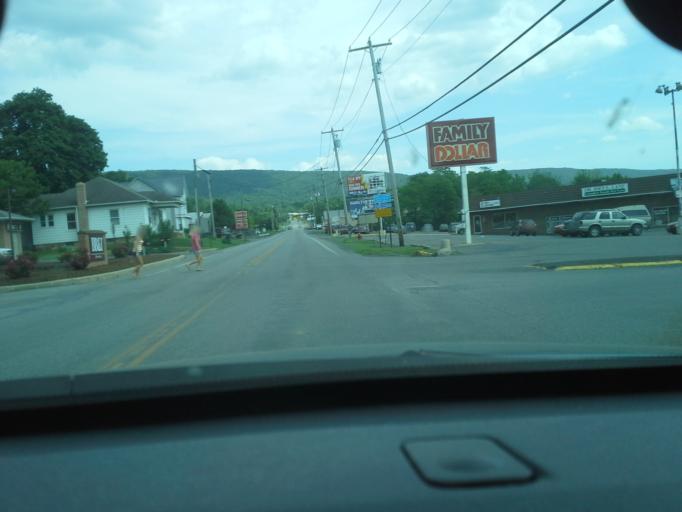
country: US
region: Pennsylvania
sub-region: Fulton County
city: McConnellsburg
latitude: 39.9285
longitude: -77.9885
